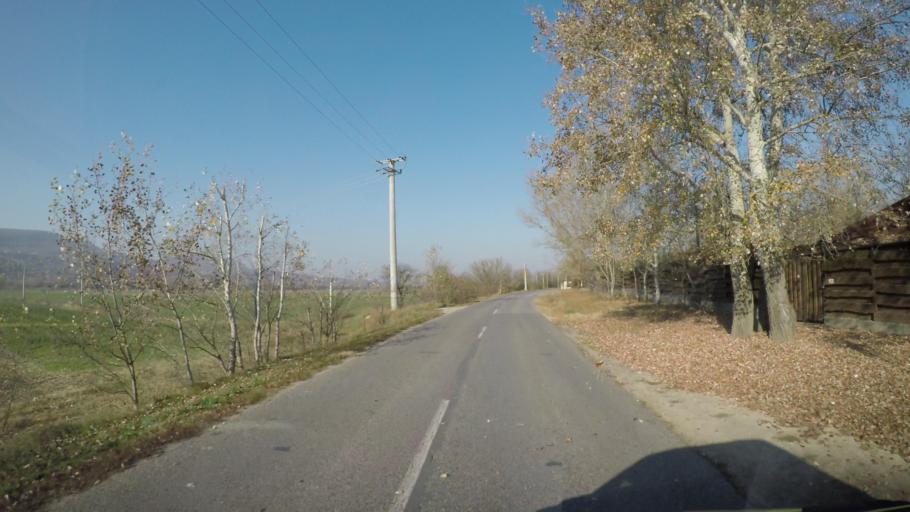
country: HU
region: Pest
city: Leanyfalu
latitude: 47.6963
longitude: 19.1039
